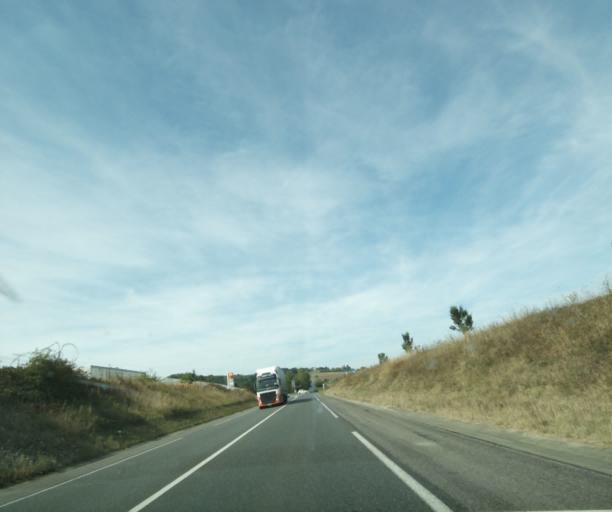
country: FR
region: Auvergne
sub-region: Departement de l'Allier
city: Saint-Germain-des-Fosses
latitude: 46.1839
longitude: 3.4558
